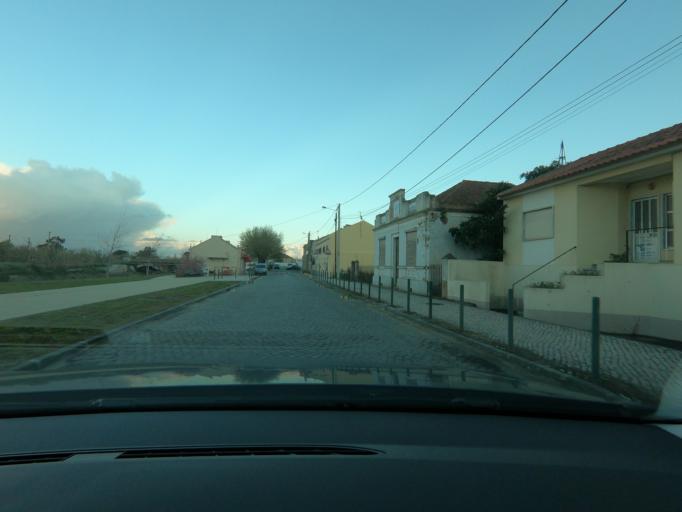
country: PT
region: Lisbon
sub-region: Vila Franca de Xira
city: Castanheira do Ribatejo
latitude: 39.0076
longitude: -8.9541
